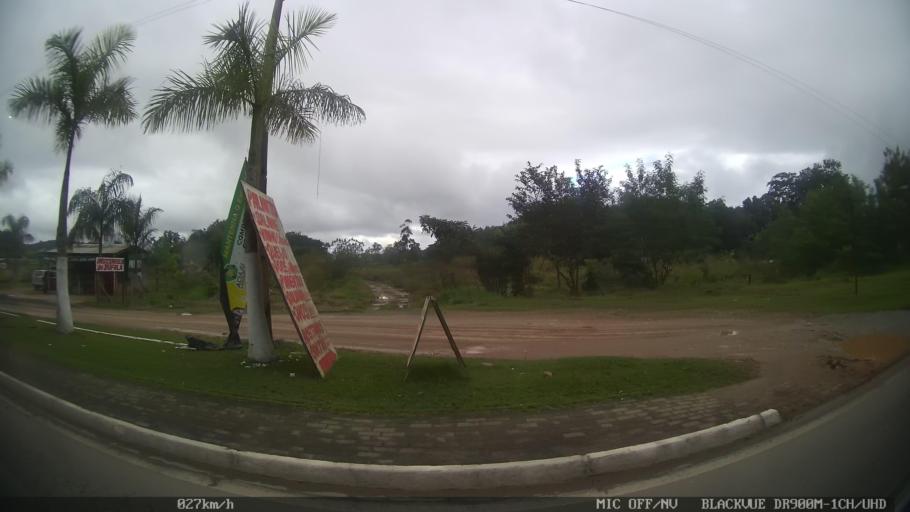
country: BR
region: Sao Paulo
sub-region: Juquia
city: Juquia
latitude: -24.3277
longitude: -47.6314
